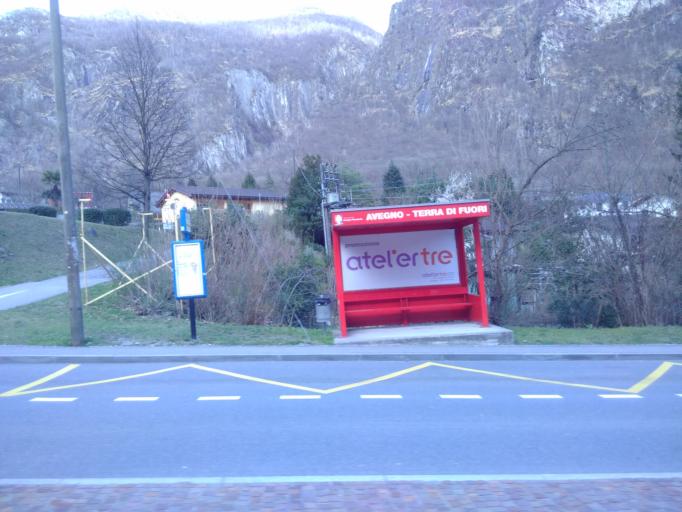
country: CH
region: Ticino
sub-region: Locarno District
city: Verscio
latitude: 46.2011
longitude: 8.7450
